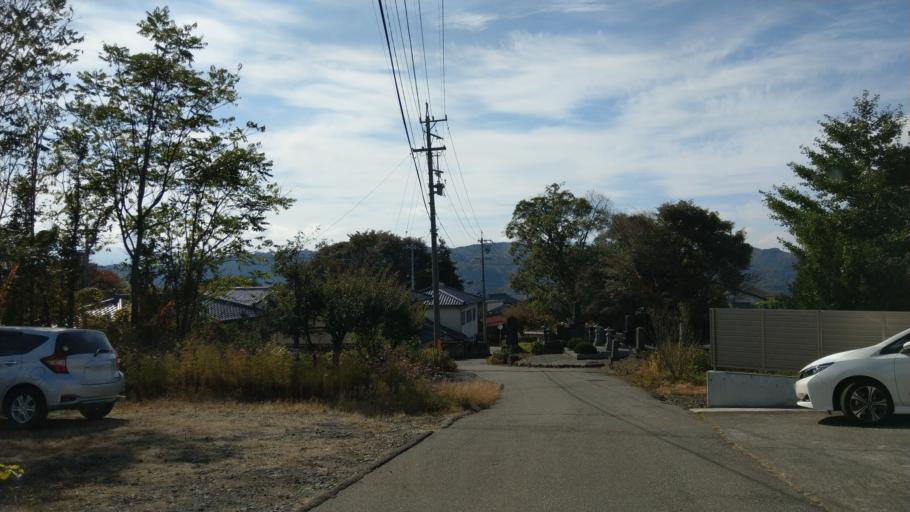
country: JP
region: Nagano
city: Komoro
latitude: 36.3242
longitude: 138.4345
